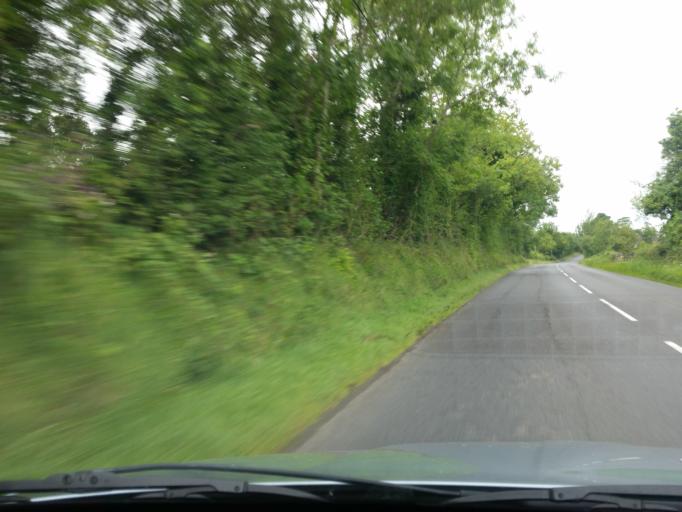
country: GB
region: Northern Ireland
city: Lisnaskea
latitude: 54.2428
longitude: -7.4489
